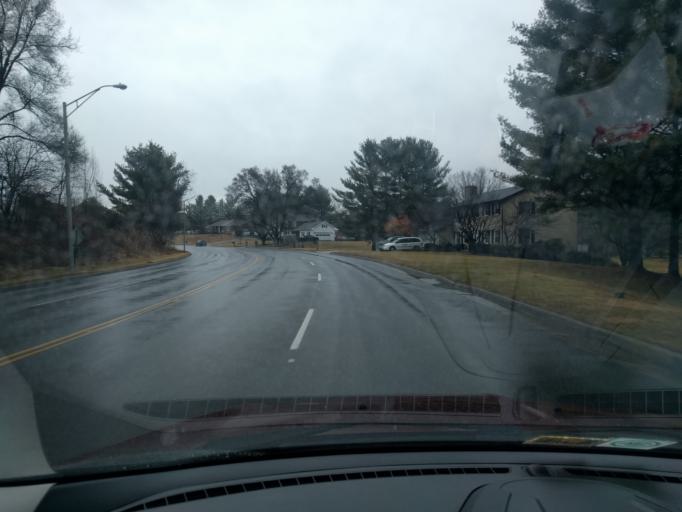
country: US
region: Virginia
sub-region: Pulaski County
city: Pulaski
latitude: 37.0583
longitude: -80.7553
